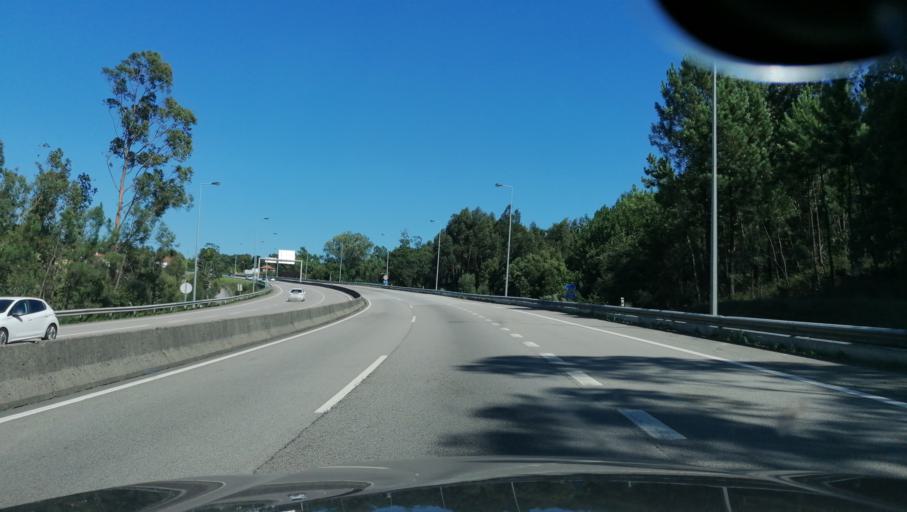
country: PT
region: Aveiro
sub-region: Santa Maria da Feira
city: Rio Meao
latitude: 40.9238
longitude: -8.5785
